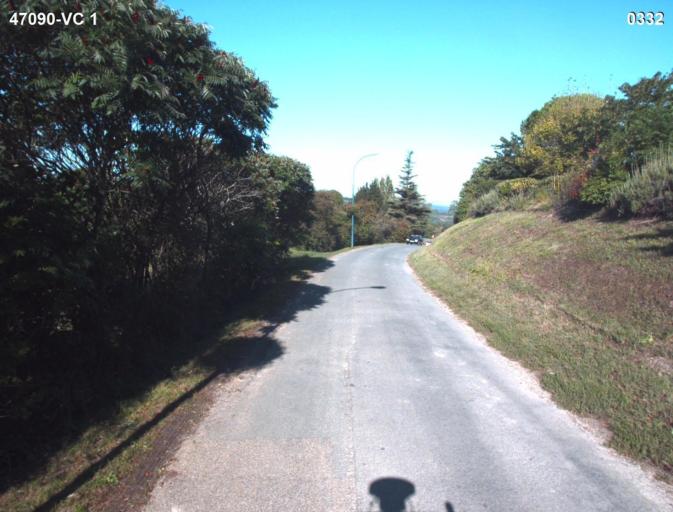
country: FR
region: Aquitaine
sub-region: Departement du Lot-et-Garonne
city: Nerac
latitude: 44.1689
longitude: 0.3760
